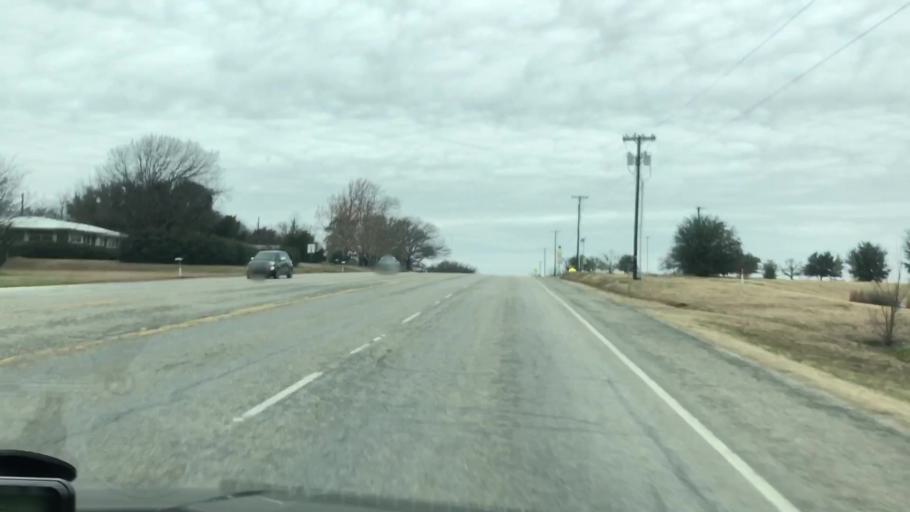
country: US
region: Texas
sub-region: Jack County
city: Jacksboro
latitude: 33.2276
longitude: -98.1670
